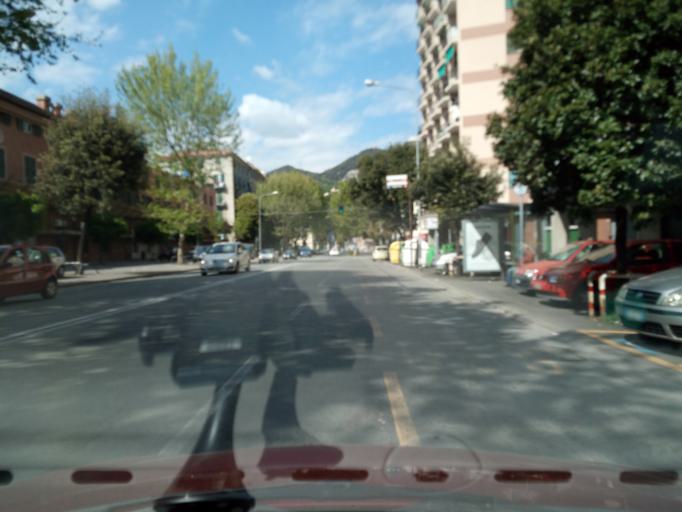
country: IT
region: Liguria
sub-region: Provincia di Genova
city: San Teodoro
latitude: 44.4241
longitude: 8.8440
